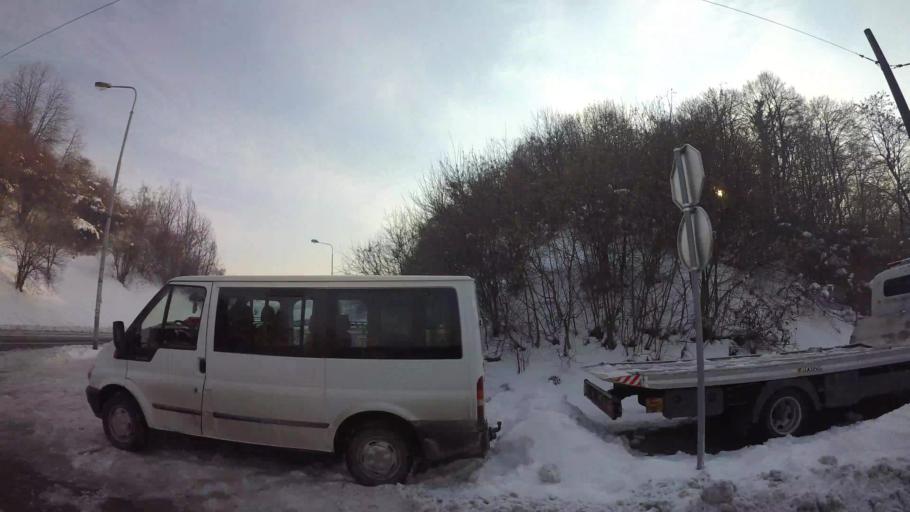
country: BA
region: Federation of Bosnia and Herzegovina
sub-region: Kanton Sarajevo
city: Sarajevo
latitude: 43.8464
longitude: 18.3672
